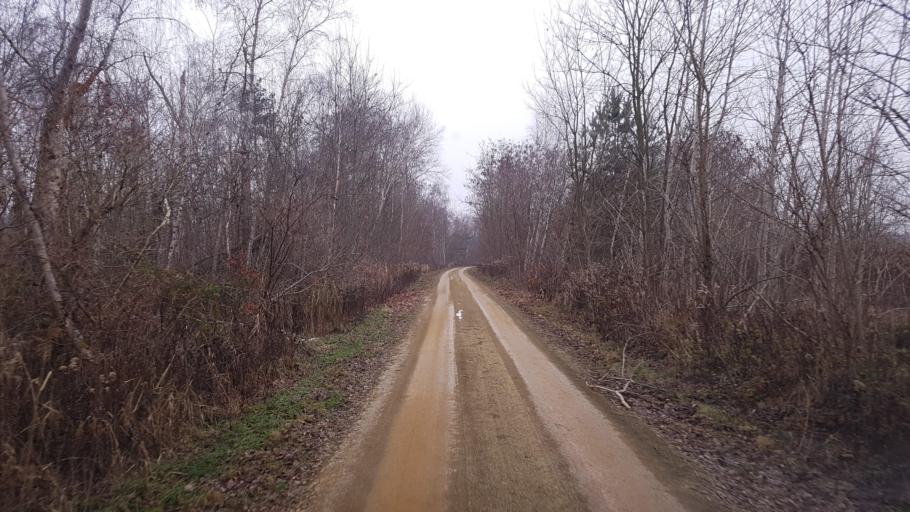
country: DE
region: Brandenburg
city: Plessa
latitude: 51.4953
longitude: 13.6580
